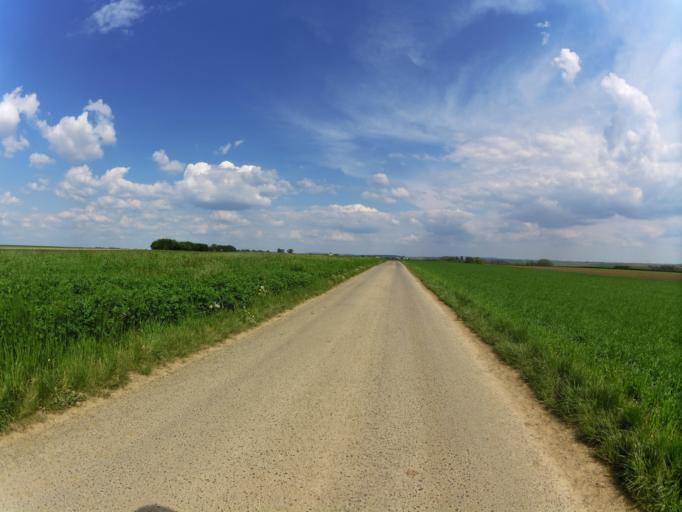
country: DE
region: Bavaria
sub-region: Regierungsbezirk Unterfranken
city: Giebelstadt
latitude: 49.6278
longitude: 9.9260
